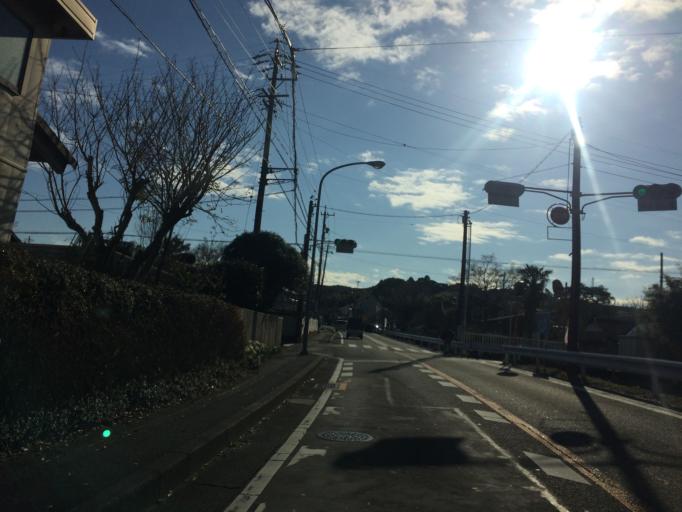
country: JP
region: Shizuoka
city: Shizuoka-shi
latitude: 34.9822
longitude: 138.4289
